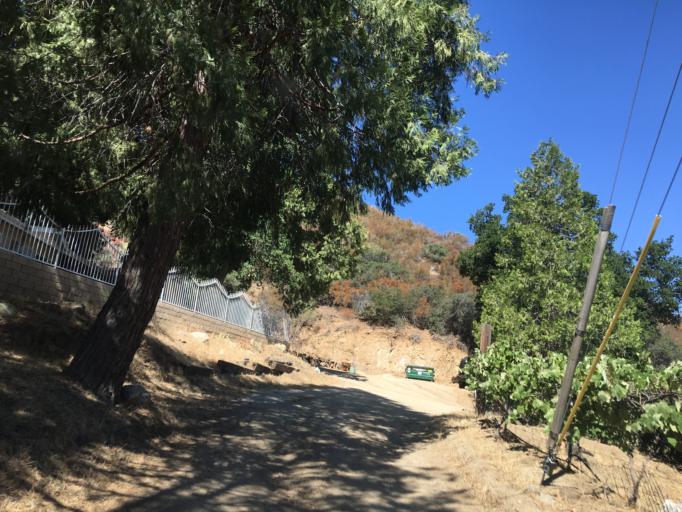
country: US
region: California
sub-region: Los Angeles County
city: Green Valley
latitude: 34.6131
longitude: -118.4027
